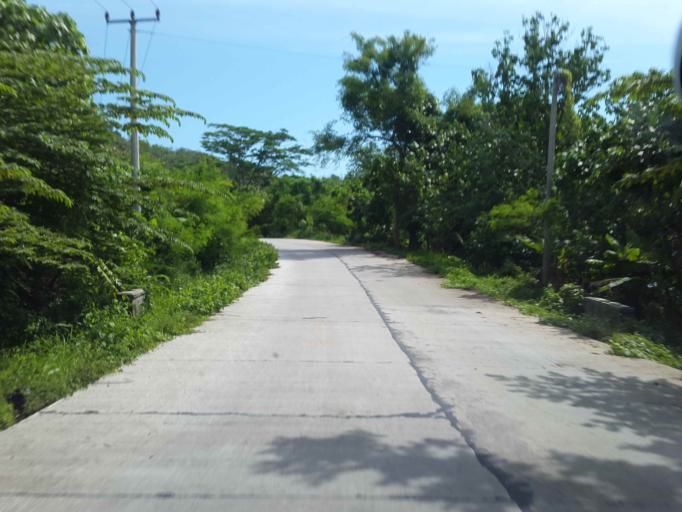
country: ID
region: Banten
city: Babakanbungur
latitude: -6.5120
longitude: 105.6353
